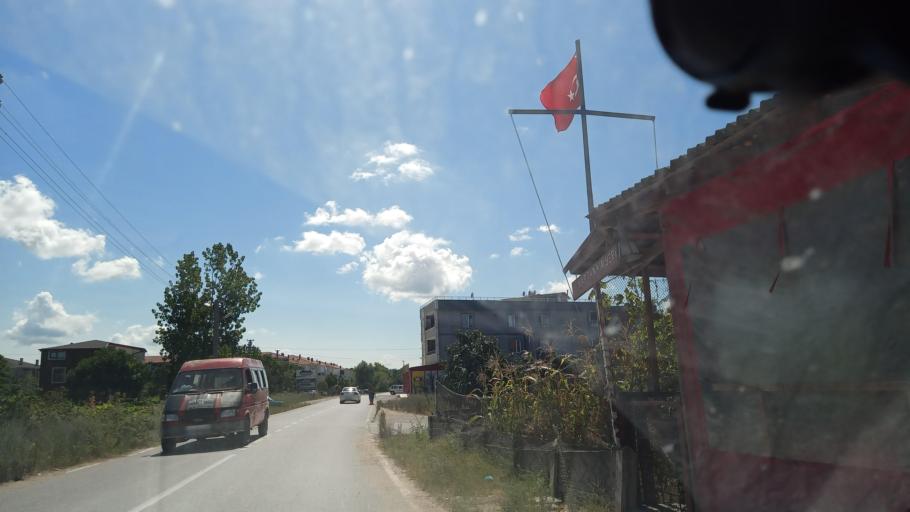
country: TR
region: Sakarya
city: Karasu
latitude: 41.1211
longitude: 30.6552
